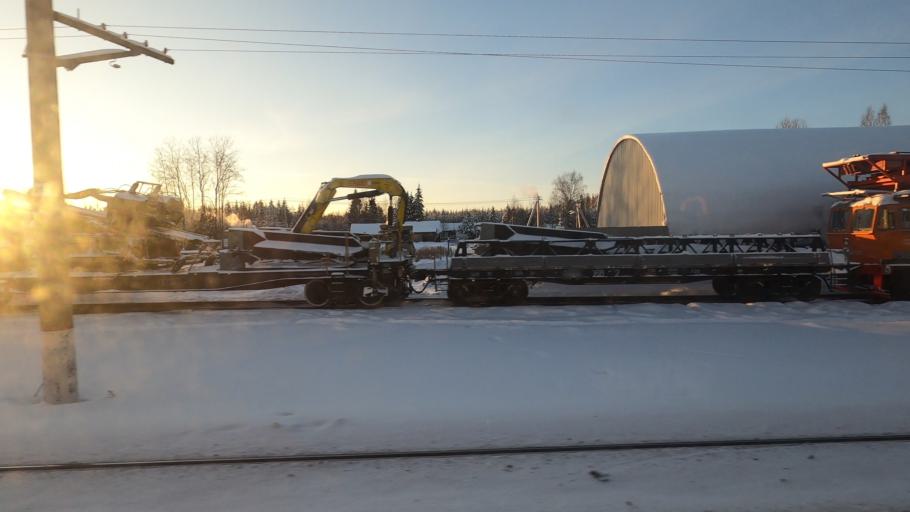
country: RU
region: Moskovskaya
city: Novo-Nikol'skoye
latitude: 56.5377
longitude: 37.5599
